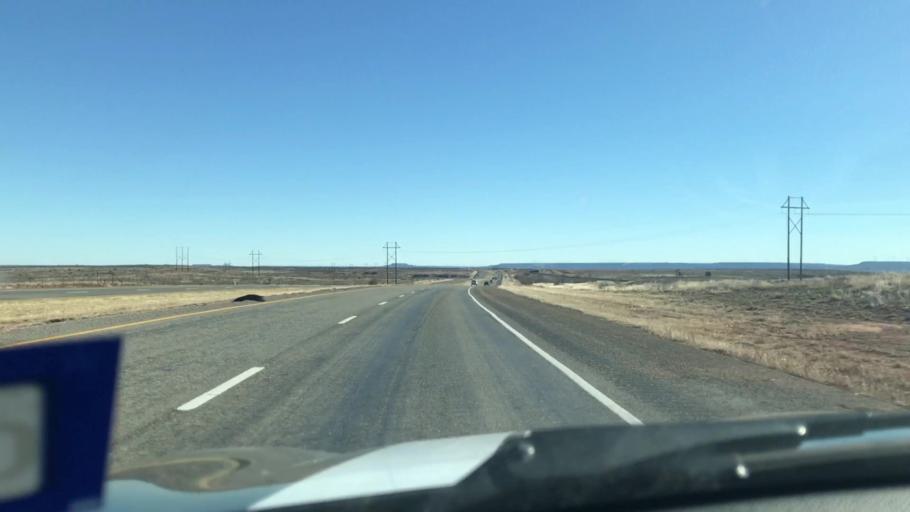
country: US
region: Texas
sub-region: Garza County
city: Post
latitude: 33.1182
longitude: -101.2790
